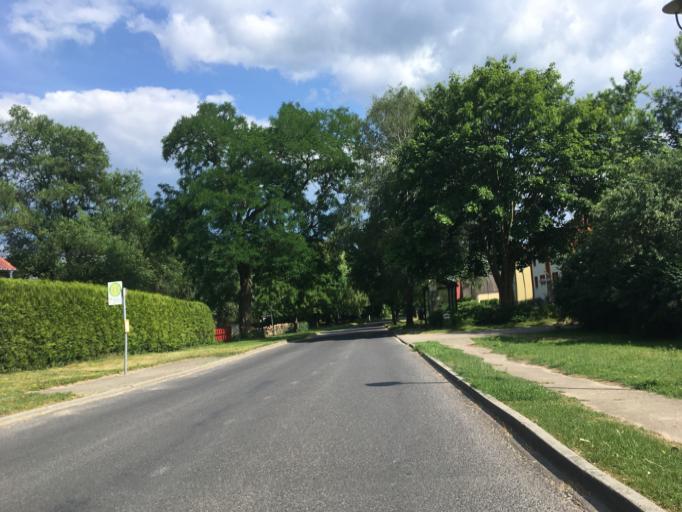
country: DE
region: Brandenburg
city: Steinhofel
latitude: 52.4206
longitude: 14.1165
